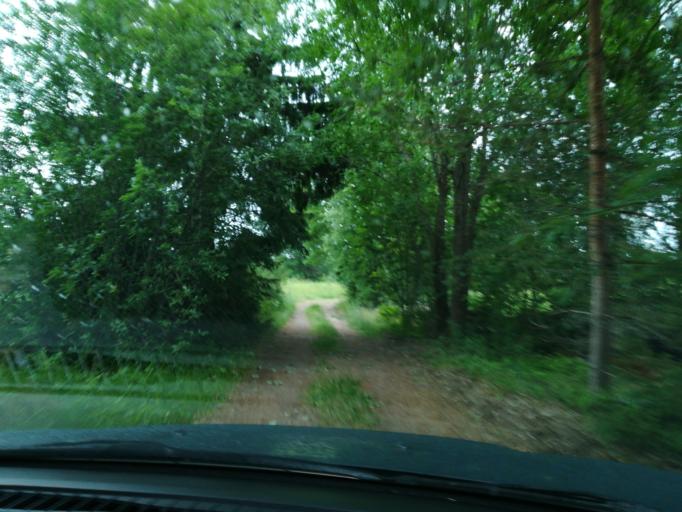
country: FI
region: South Karelia
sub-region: Lappeenranta
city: Savitaipale
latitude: 61.1816
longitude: 27.5496
